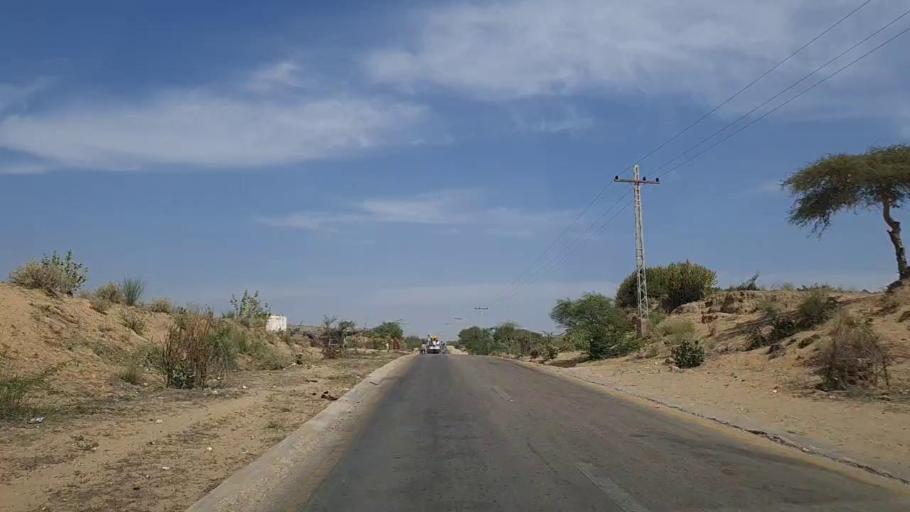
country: PK
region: Sindh
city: Mithi
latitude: 24.7654
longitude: 69.7974
